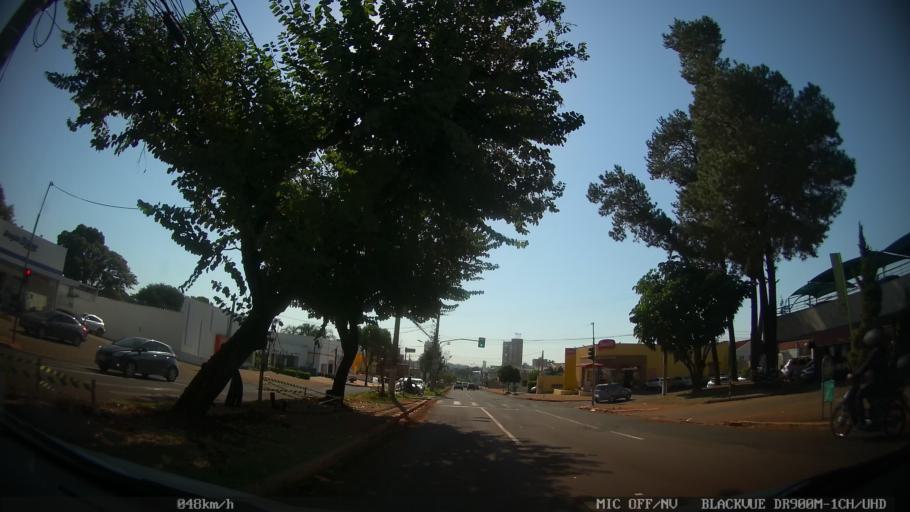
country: BR
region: Sao Paulo
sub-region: Ribeirao Preto
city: Ribeirao Preto
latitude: -21.1920
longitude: -47.8103
